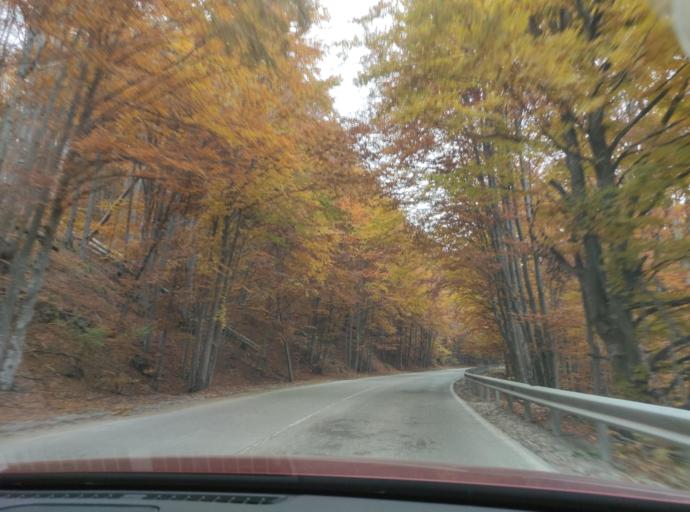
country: BG
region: Sofiya
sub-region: Obshtina Godech
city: Godech
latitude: 43.1154
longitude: 23.1120
